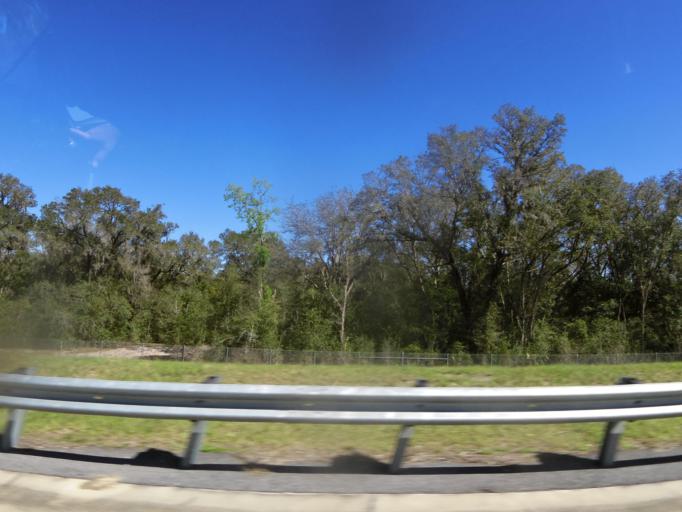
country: US
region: Florida
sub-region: Lake County
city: Mount Plymouth
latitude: 28.7919
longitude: -81.5794
